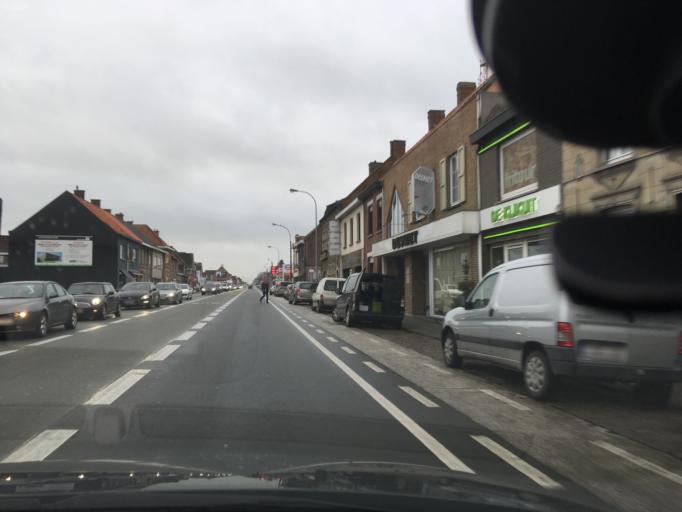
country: BE
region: Flanders
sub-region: Provincie West-Vlaanderen
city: Roeselare
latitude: 50.9348
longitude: 3.1206
